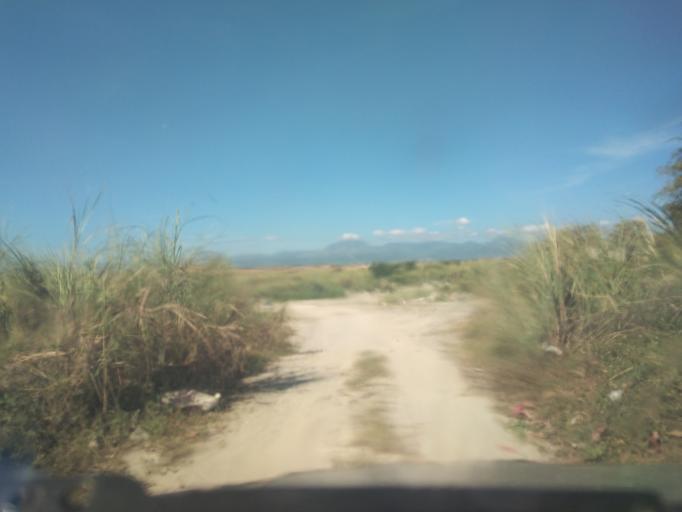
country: PH
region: Central Luzon
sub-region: Province of Pampanga
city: Calibutbut
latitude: 15.0829
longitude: 120.6068
